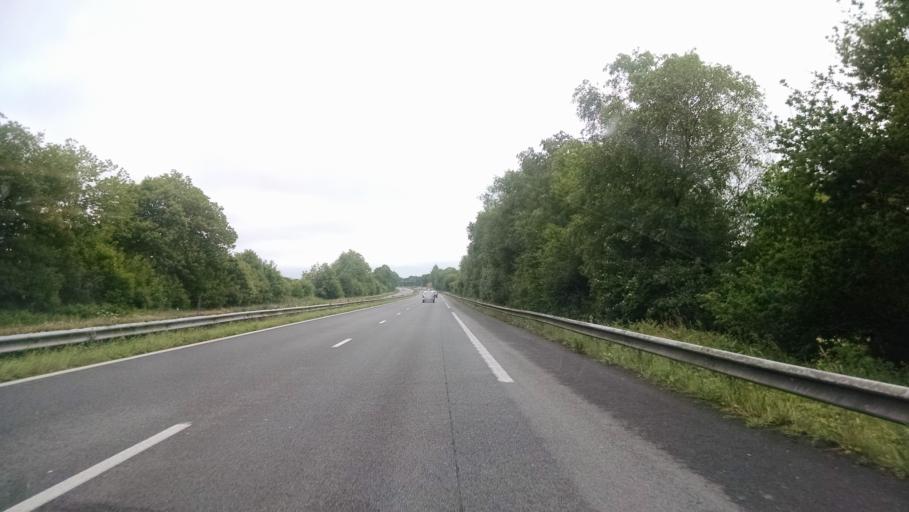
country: FR
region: Brittany
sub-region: Departement du Finistere
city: Saint-Yvi
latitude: 47.9553
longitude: -3.9500
